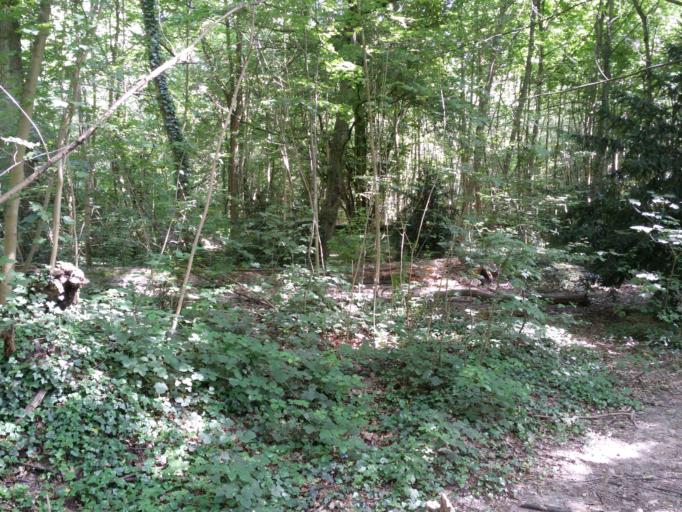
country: FR
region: Ile-de-France
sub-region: Departement des Hauts-de-Seine
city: Sevres
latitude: 48.8299
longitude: 2.2112
